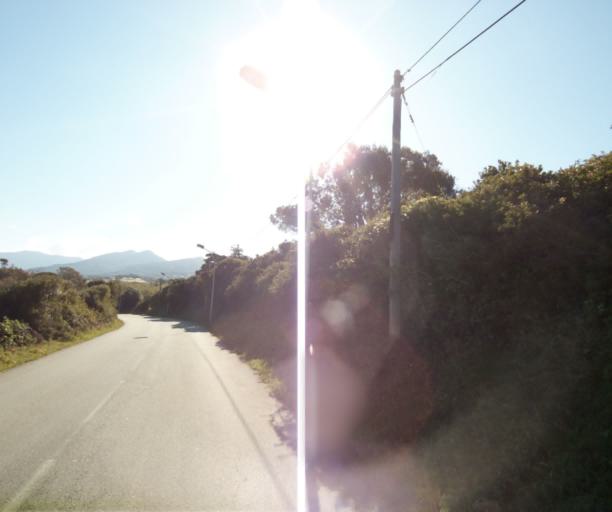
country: FR
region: Corsica
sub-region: Departement de la Corse-du-Sud
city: Propriano
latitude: 41.6727
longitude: 8.8952
